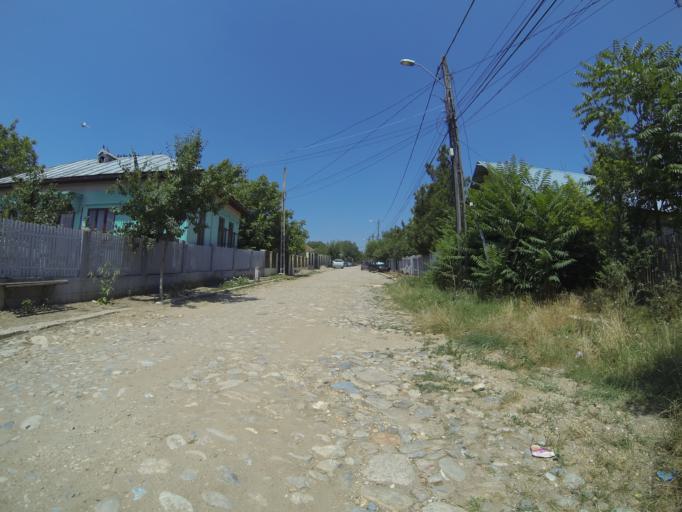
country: RO
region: Dolj
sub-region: Comuna Segarcea
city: Segarcea
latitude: 44.0905
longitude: 23.7501
